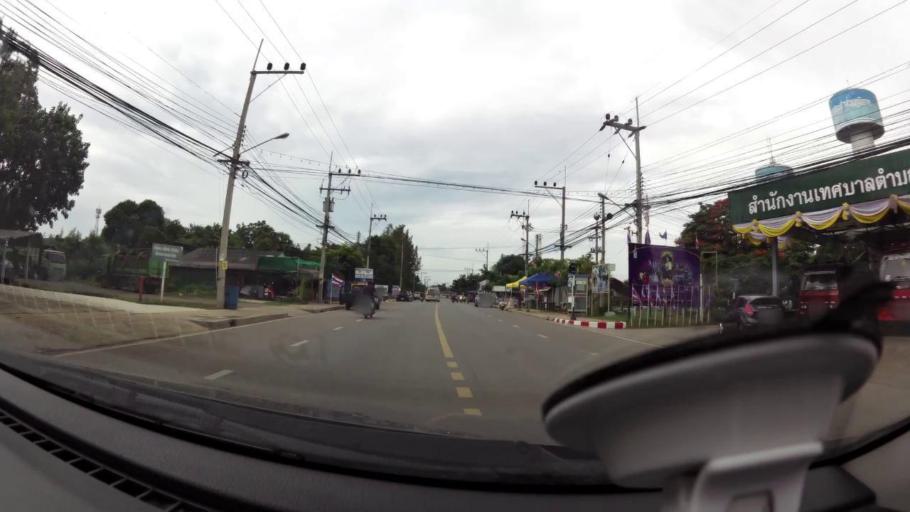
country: TH
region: Prachuap Khiri Khan
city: Pran Buri
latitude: 12.3938
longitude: 99.9881
